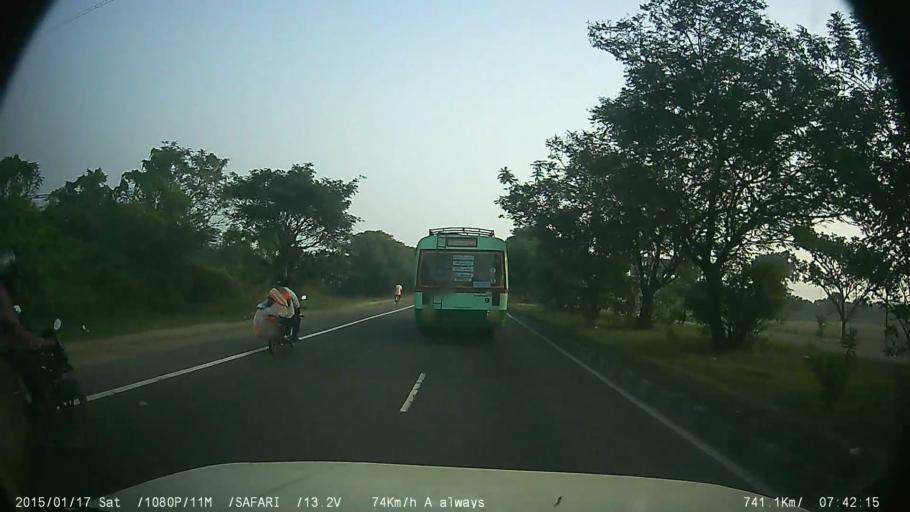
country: IN
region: Tamil Nadu
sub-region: Kancheepuram
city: Singapperumalkovil
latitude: 12.8028
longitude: 80.0251
